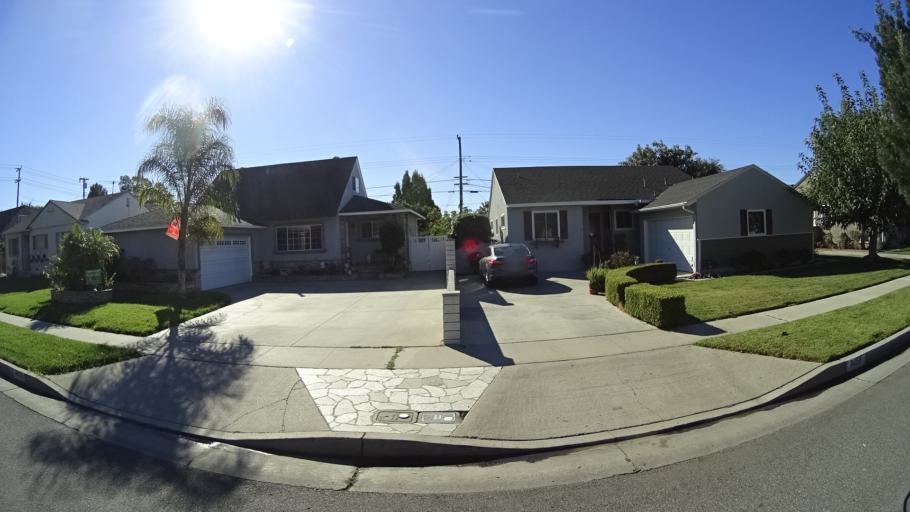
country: US
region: California
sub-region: Orange County
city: Buena Park
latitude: 33.8541
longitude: -117.9858
